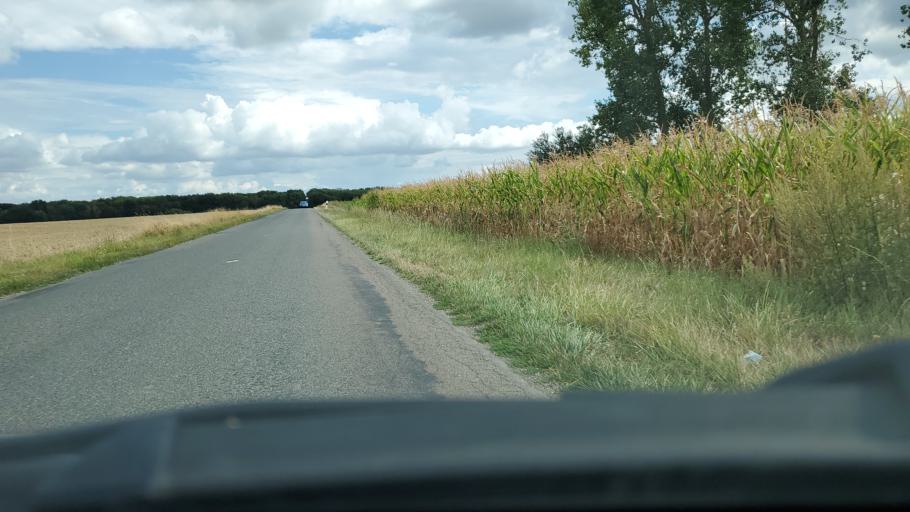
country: FR
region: Ile-de-France
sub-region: Departement de Seine-et-Marne
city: Pommeuse
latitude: 48.8648
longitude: 3.0010
